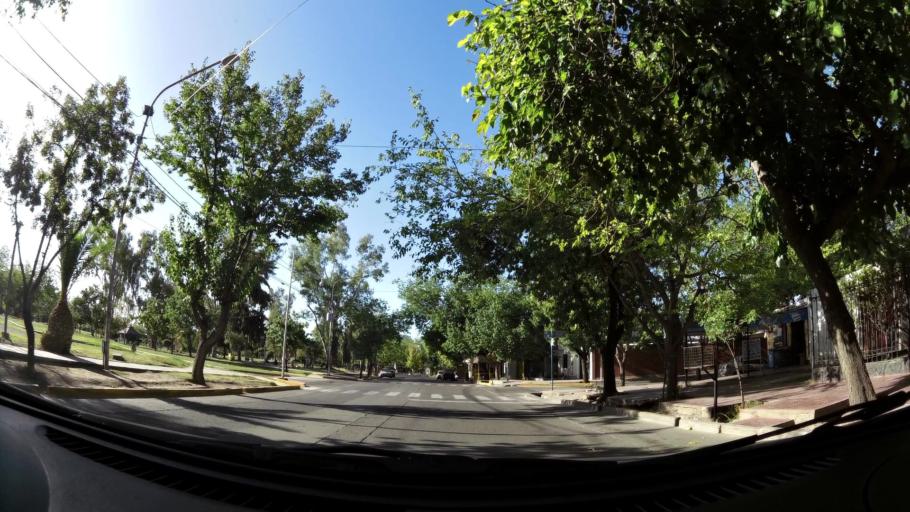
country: AR
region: Mendoza
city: Villa Nueva
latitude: -32.9068
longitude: -68.8002
